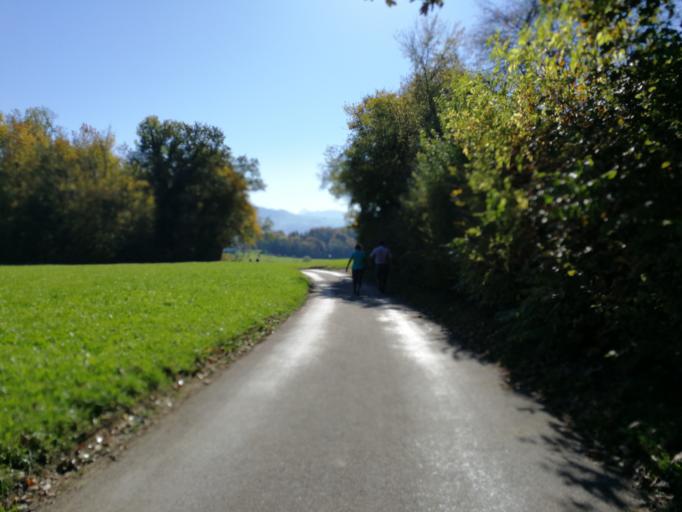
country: CH
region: Zurich
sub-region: Bezirk Meilen
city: Hombrechtikon
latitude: 47.2651
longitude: 8.7789
